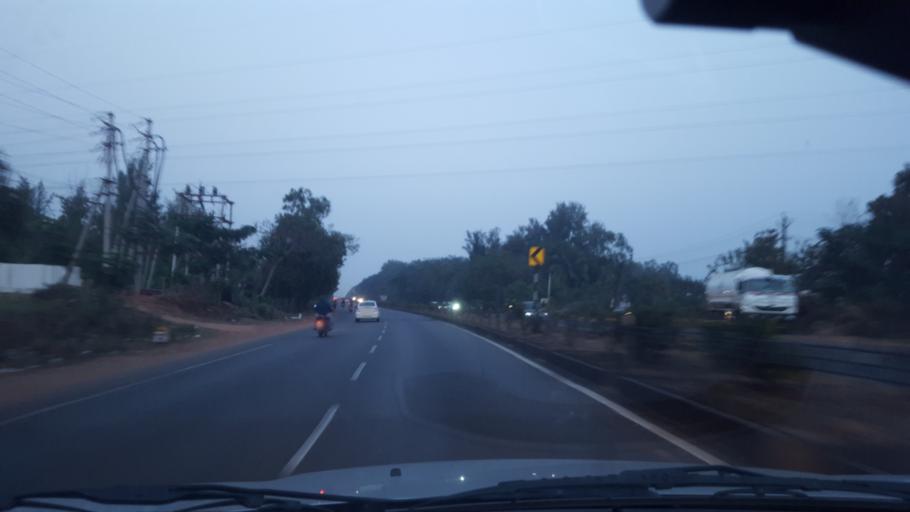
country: IN
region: Andhra Pradesh
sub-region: East Godavari
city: Rajahmundry
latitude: 17.0282
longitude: 81.8149
